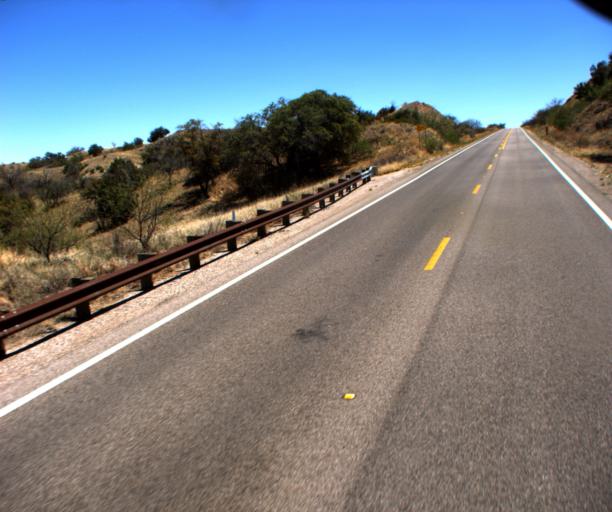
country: US
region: Arizona
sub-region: Pima County
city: Corona de Tucson
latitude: 31.7783
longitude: -110.6903
